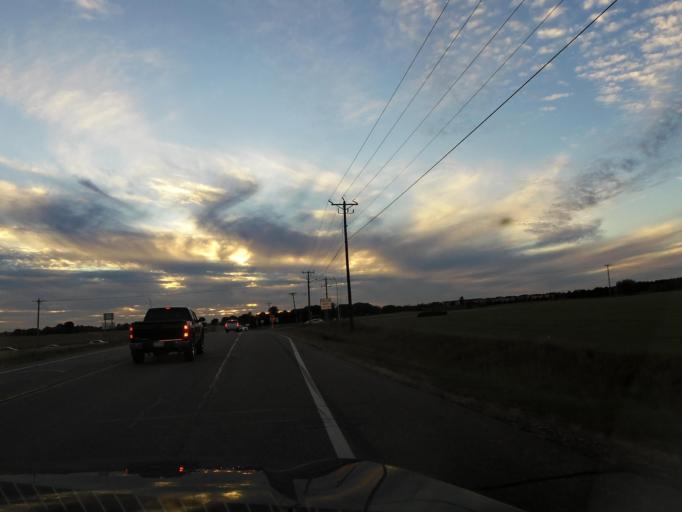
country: US
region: Minnesota
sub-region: Washington County
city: Afton
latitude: 44.8912
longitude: -92.8606
